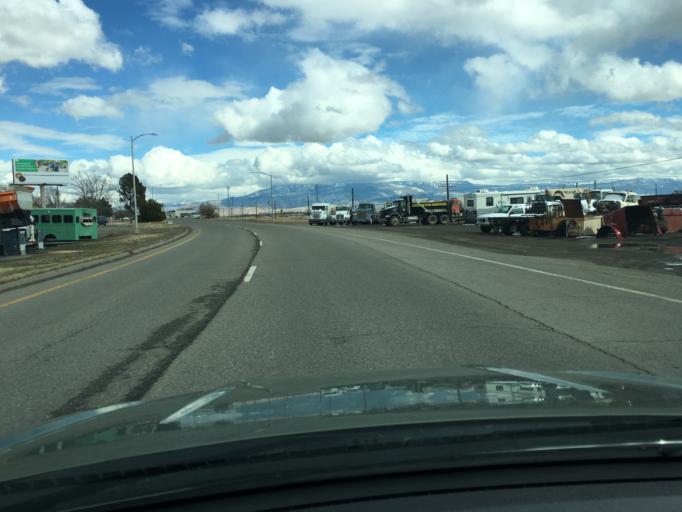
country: US
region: Colorado
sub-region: Mesa County
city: Grand Junction
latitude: 39.0644
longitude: -108.5506
